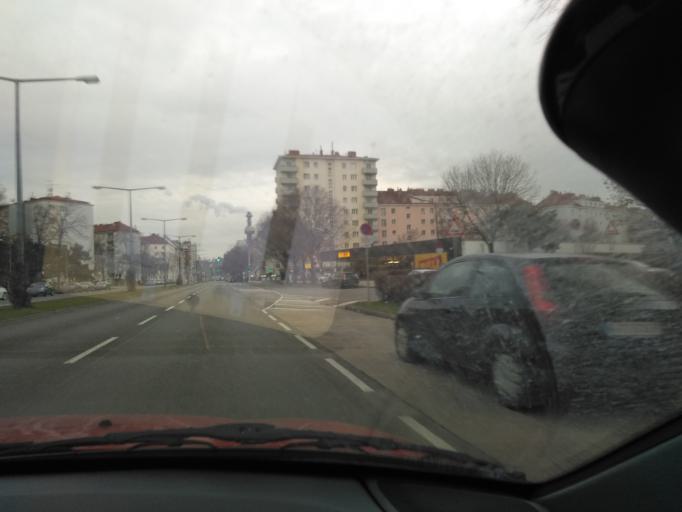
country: AT
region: Vienna
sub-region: Wien Stadt
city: Vienna
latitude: 48.2401
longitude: 16.3698
